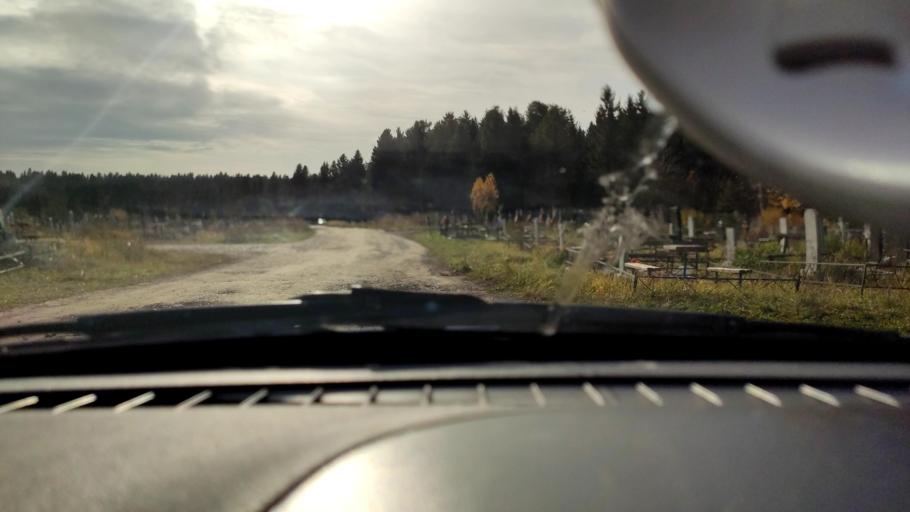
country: RU
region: Perm
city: Kultayevo
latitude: 57.8579
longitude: 55.8691
